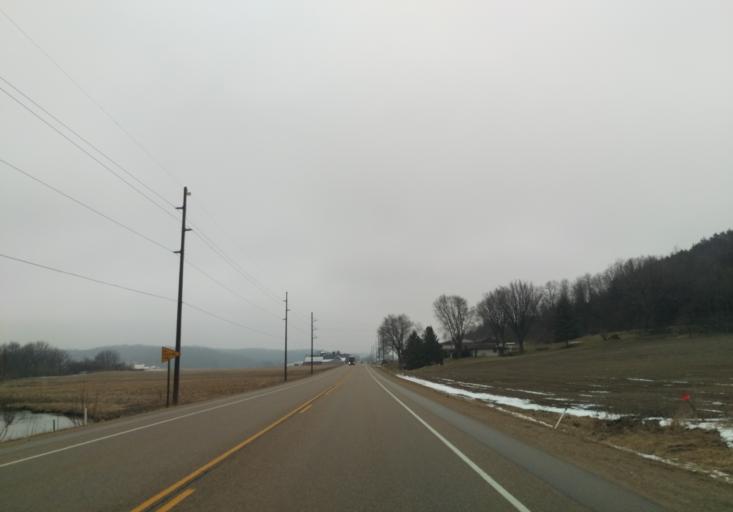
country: US
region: Wisconsin
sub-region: Dane County
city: Black Earth
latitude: 43.1471
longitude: -89.7587
